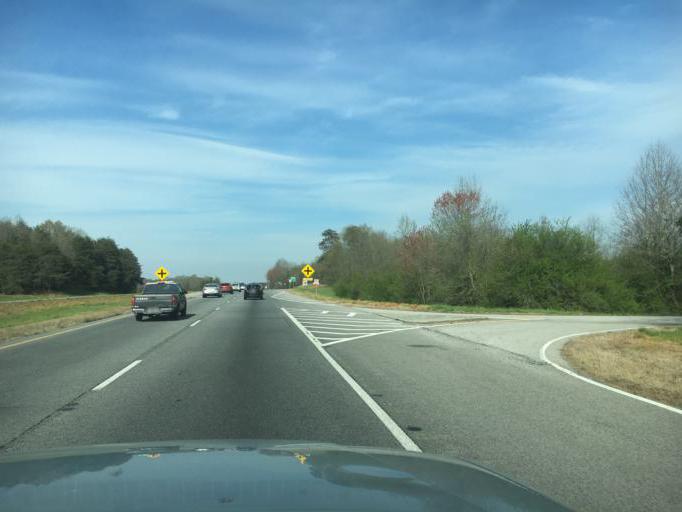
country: US
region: Georgia
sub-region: Hall County
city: Lula
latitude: 34.4077
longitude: -83.6705
